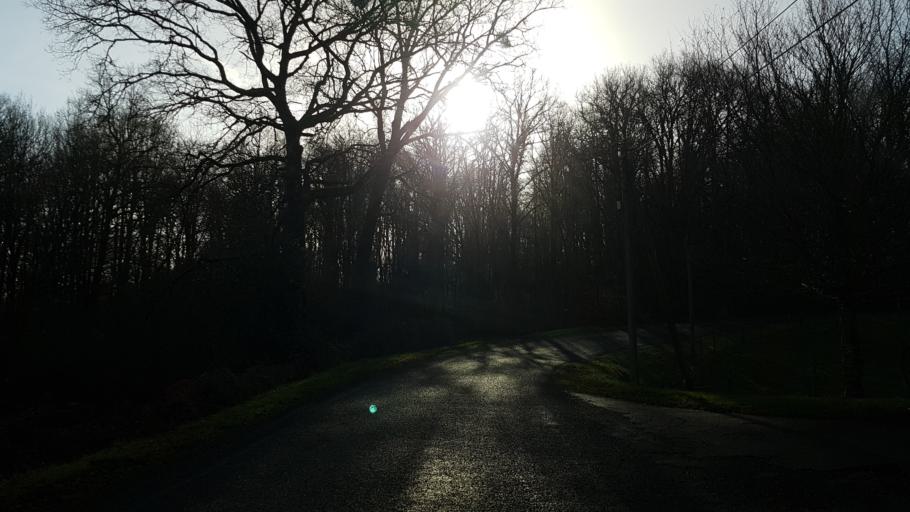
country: FR
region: Poitou-Charentes
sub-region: Departement de la Charente
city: Etagnac
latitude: 45.8981
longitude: 0.8063
